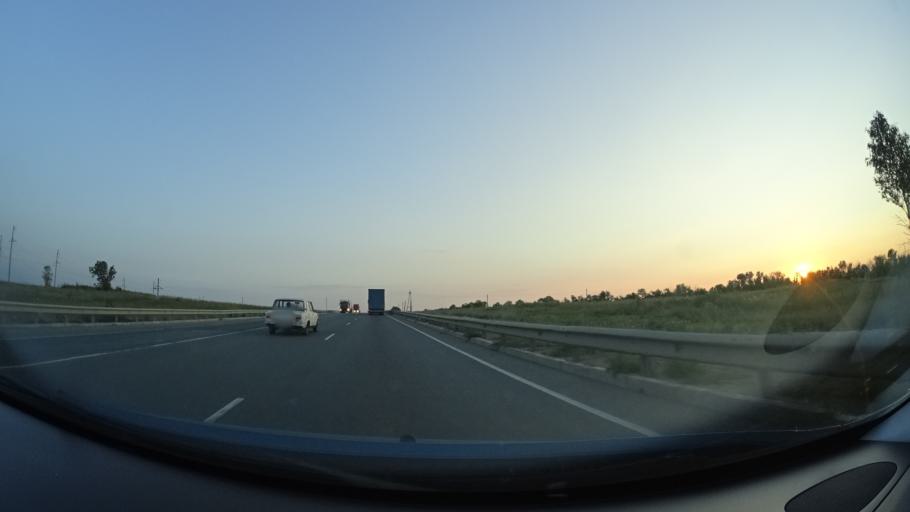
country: RU
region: Samara
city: Sukhodol
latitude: 53.8621
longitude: 51.1776
